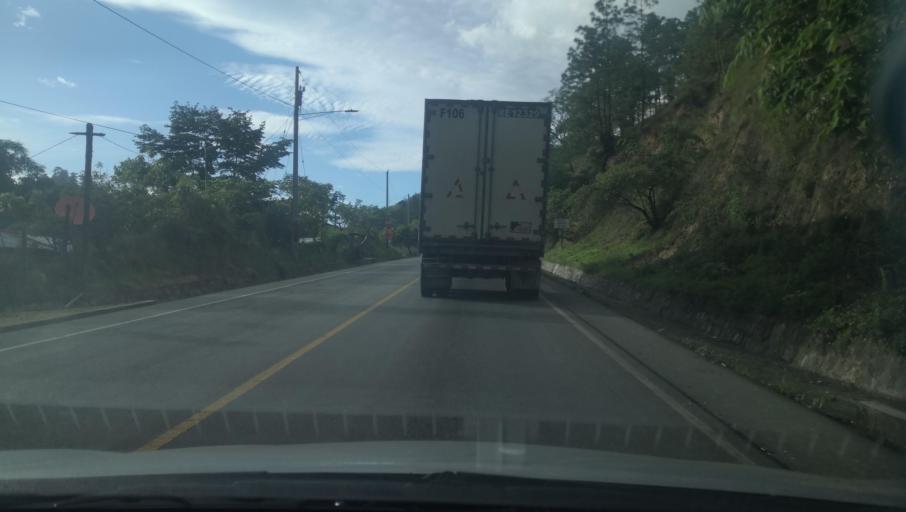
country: NI
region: Nueva Segovia
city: Mozonte
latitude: 13.7185
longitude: -86.5048
